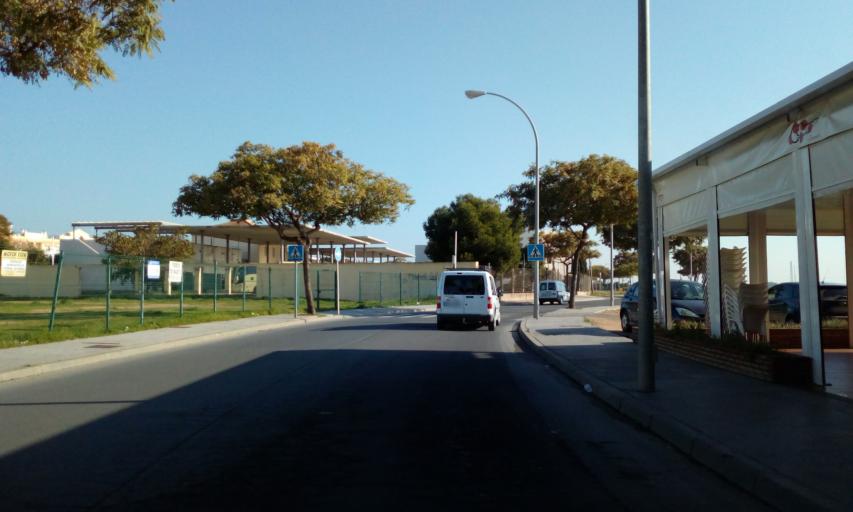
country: ES
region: Andalusia
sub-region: Provincia de Huelva
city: Ayamonte
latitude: 37.2141
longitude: -7.4005
